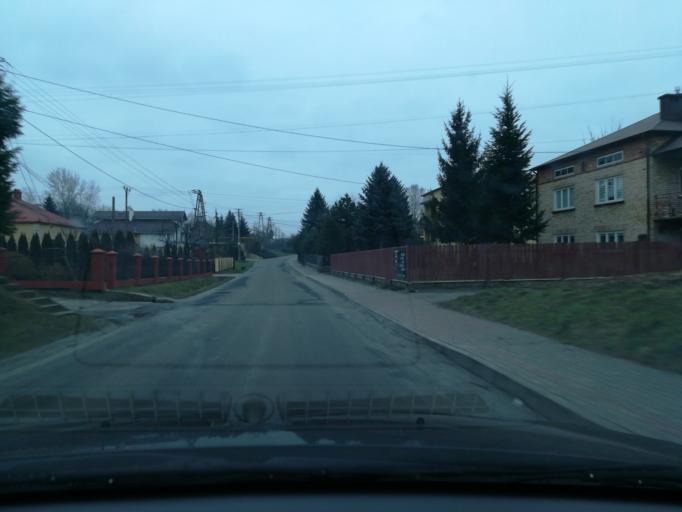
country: PL
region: Subcarpathian Voivodeship
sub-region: Powiat lancucki
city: Kosina
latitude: 50.0785
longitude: 22.3253
